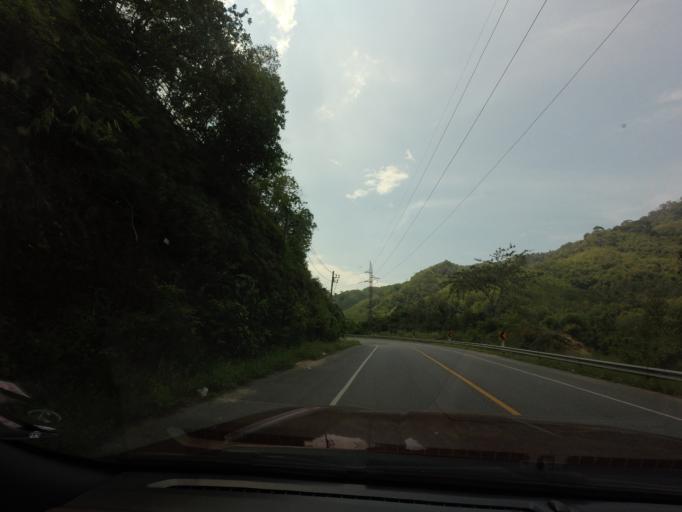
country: TH
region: Yala
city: Than To
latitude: 5.9971
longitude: 101.1920
